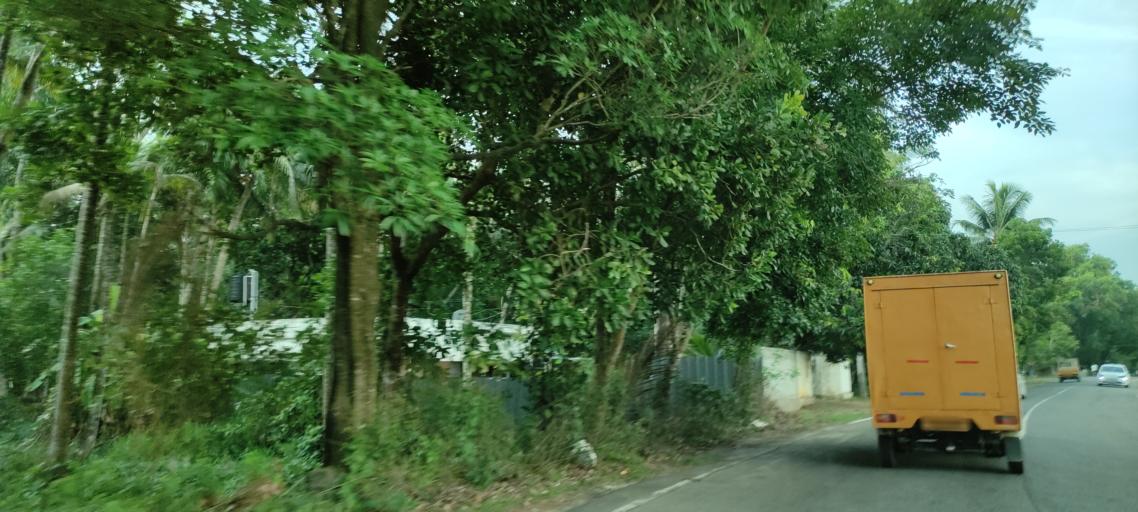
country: IN
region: Kerala
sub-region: Kottayam
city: Vaikam
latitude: 9.7637
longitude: 76.3632
